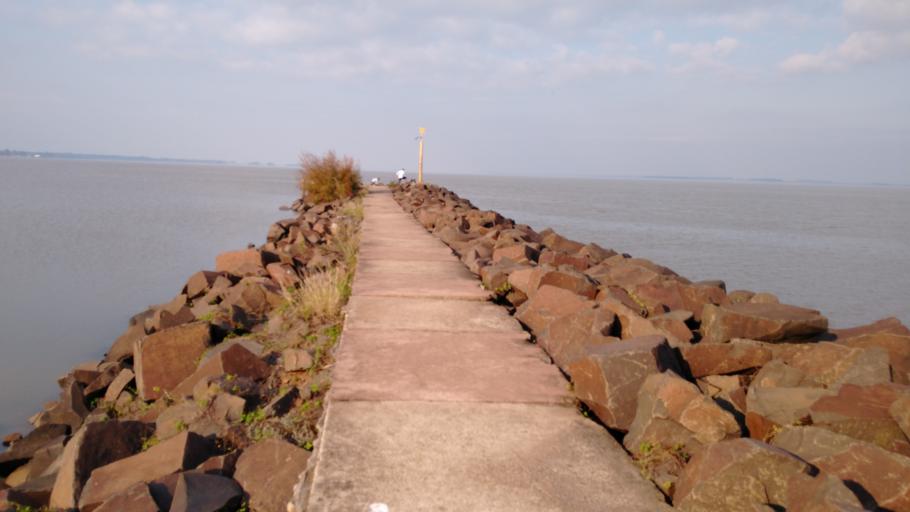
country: AR
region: Entre Rios
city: Santa Ana
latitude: -30.9141
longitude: -57.9250
